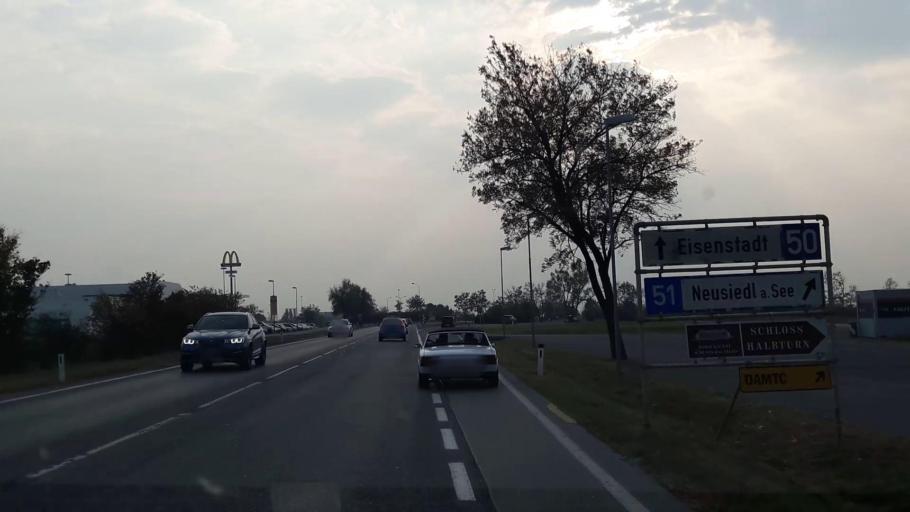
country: AT
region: Burgenland
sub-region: Politischer Bezirk Neusiedl am See
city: Neusiedl am See
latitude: 47.9751
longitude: 16.8411
